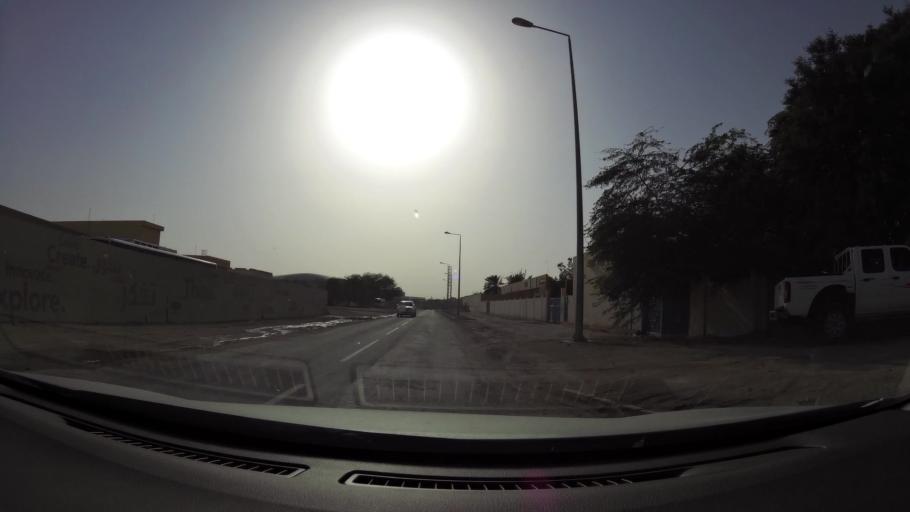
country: QA
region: Baladiyat ar Rayyan
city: Ar Rayyan
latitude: 25.3278
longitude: 51.4435
